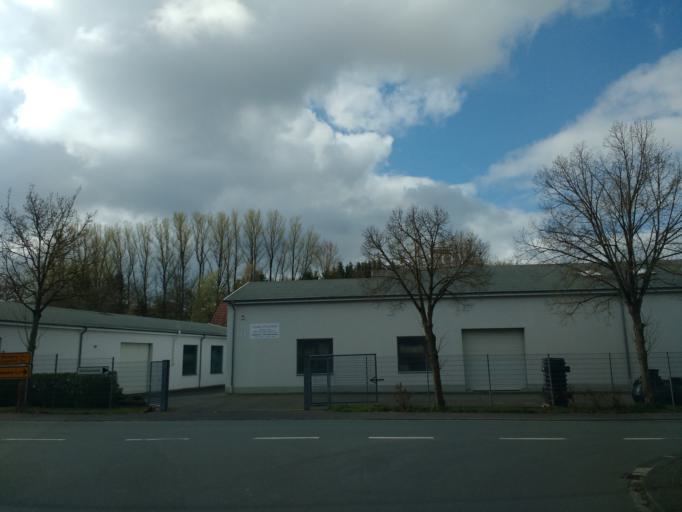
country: DE
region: North Rhine-Westphalia
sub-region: Regierungsbezirk Detmold
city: Wunnenberg
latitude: 51.5099
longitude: 8.7454
